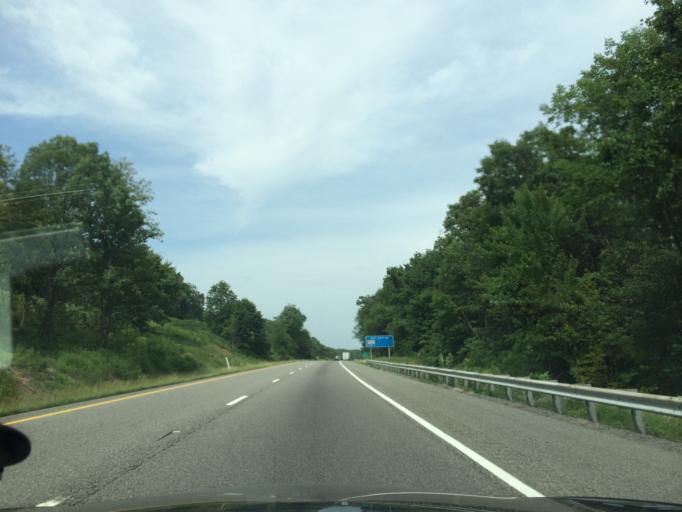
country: US
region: West Virginia
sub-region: Morgan County
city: Berkeley Springs
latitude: 39.6878
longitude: -78.4017
